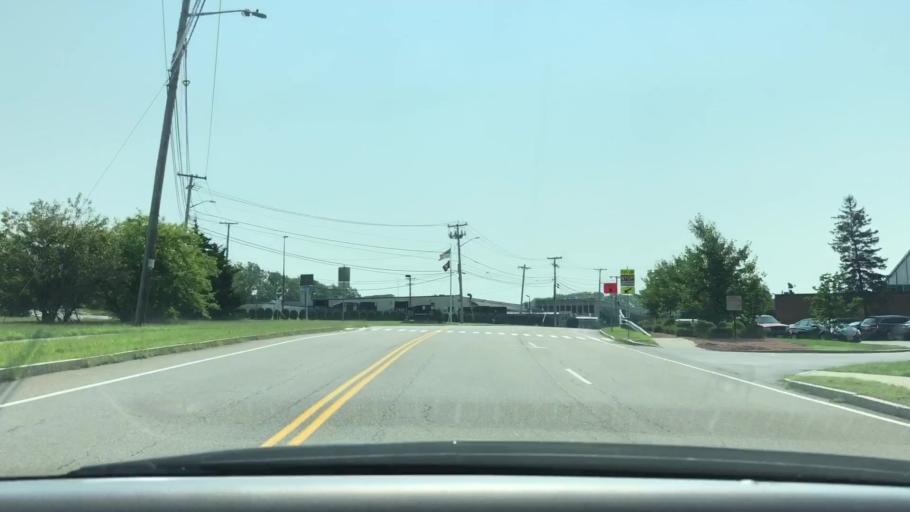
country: US
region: Massachusetts
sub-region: Norfolk County
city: Norwood
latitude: 42.2091
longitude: -71.1807
